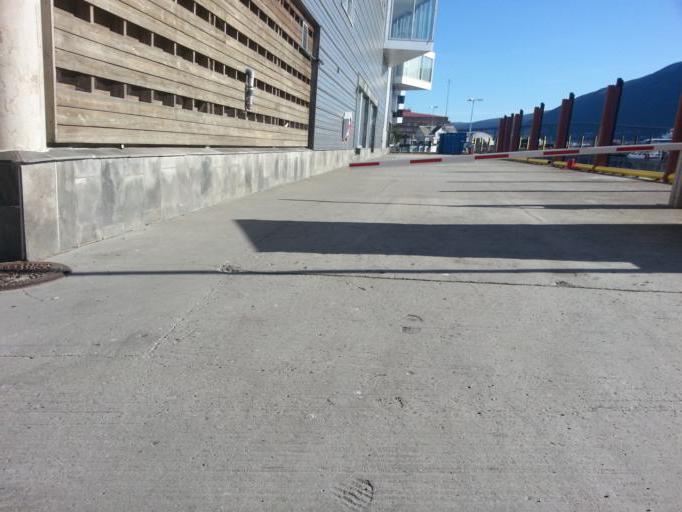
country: NO
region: Troms
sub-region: Tromso
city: Tromso
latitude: 69.6461
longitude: 18.9545
